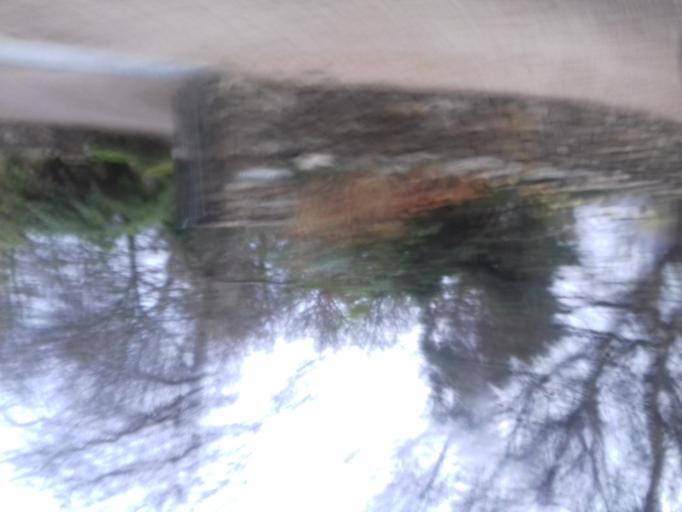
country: IE
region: Ulster
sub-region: County Donegal
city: Buncrana
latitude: 55.2220
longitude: -7.6118
